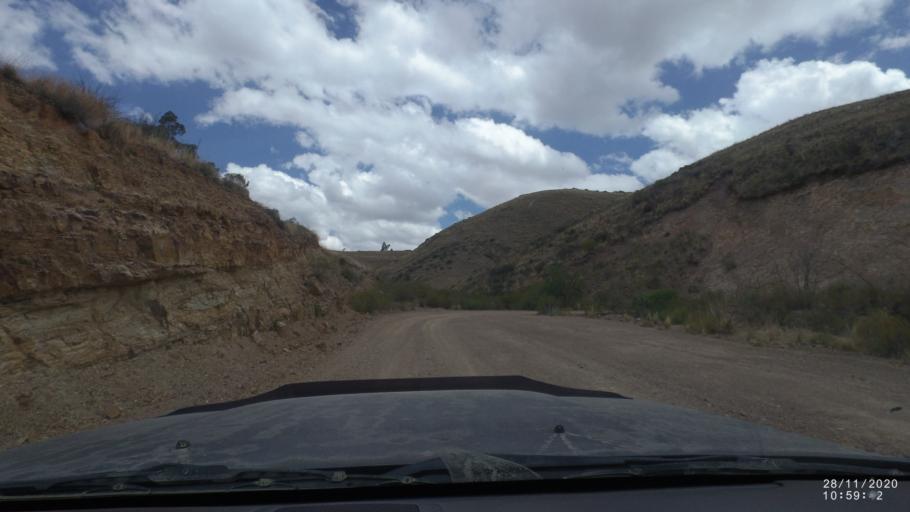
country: BO
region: Cochabamba
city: Capinota
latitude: -17.7715
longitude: -66.1084
